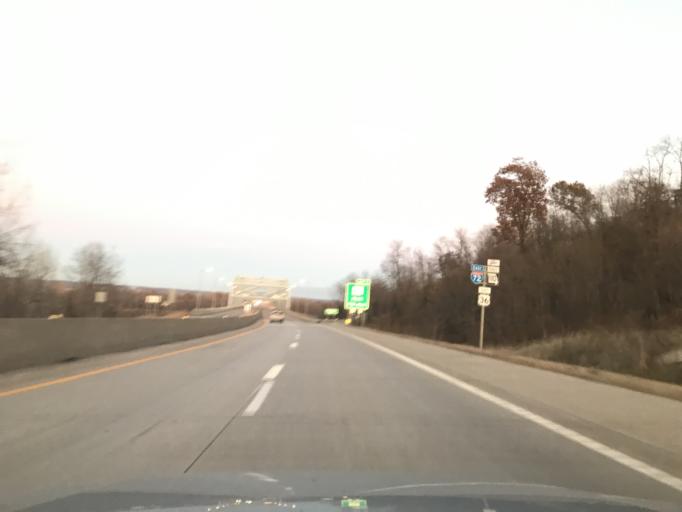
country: US
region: Missouri
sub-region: Marion County
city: Hannibal
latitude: 39.7184
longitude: -91.3638
